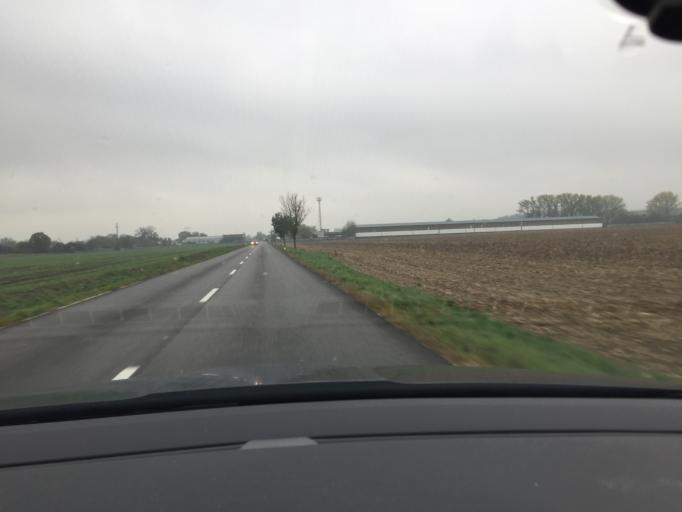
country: SK
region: Nitriansky
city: Zeliezovce
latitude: 48.0298
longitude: 18.8020
